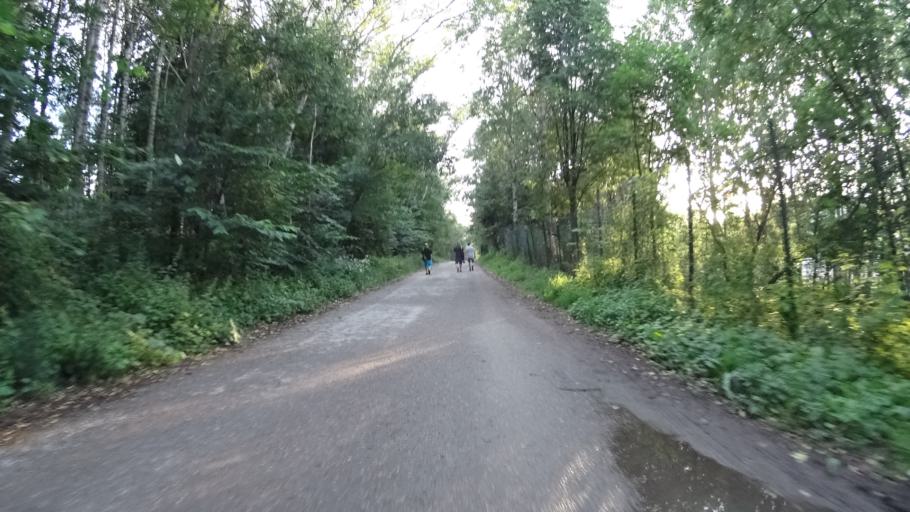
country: FI
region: Uusimaa
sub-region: Helsinki
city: Teekkarikylae
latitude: 60.2138
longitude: 24.8446
